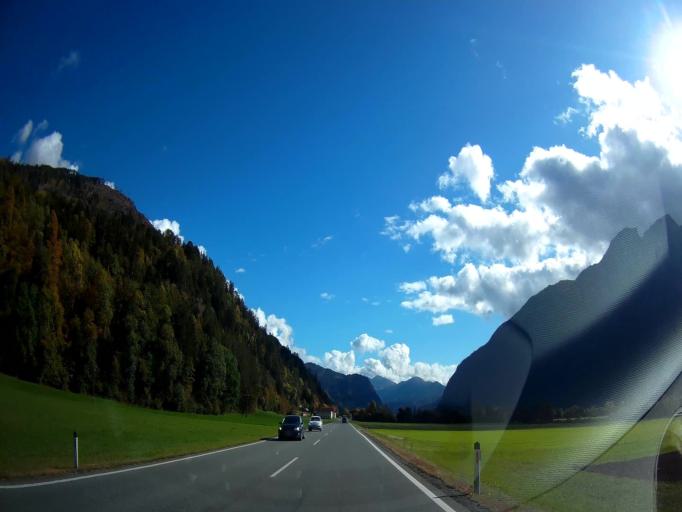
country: AT
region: Tyrol
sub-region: Politischer Bezirk Lienz
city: Lavant
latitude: 46.8108
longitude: 12.8497
